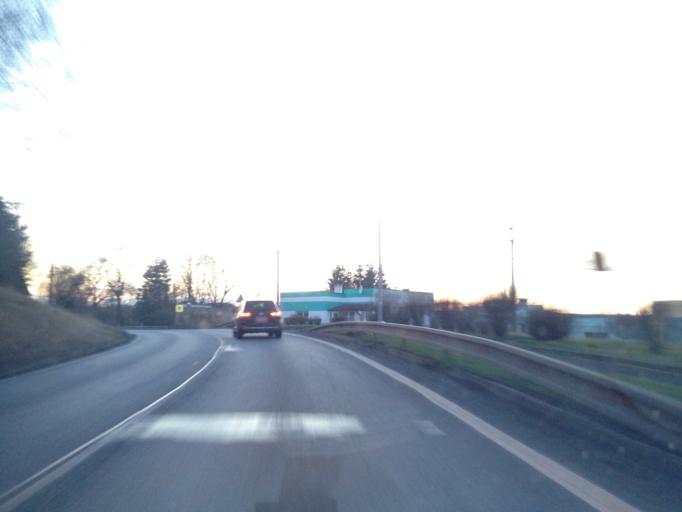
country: CZ
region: Central Bohemia
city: Jesenice
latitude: 50.1556
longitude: 13.5272
